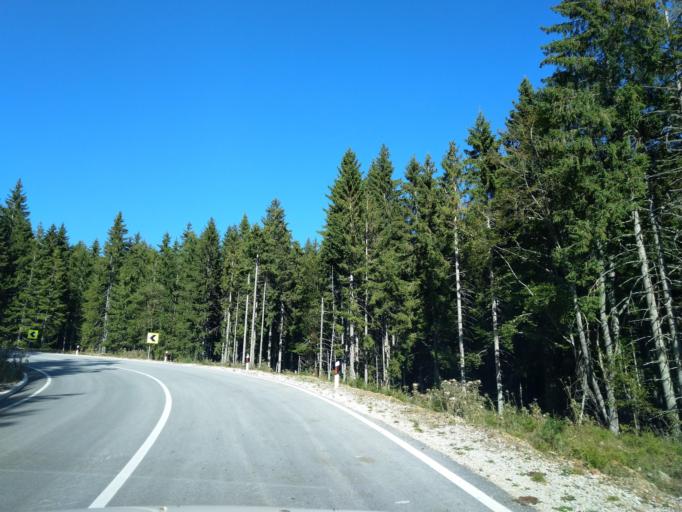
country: RS
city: Sokolovica
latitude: 43.3017
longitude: 20.3089
